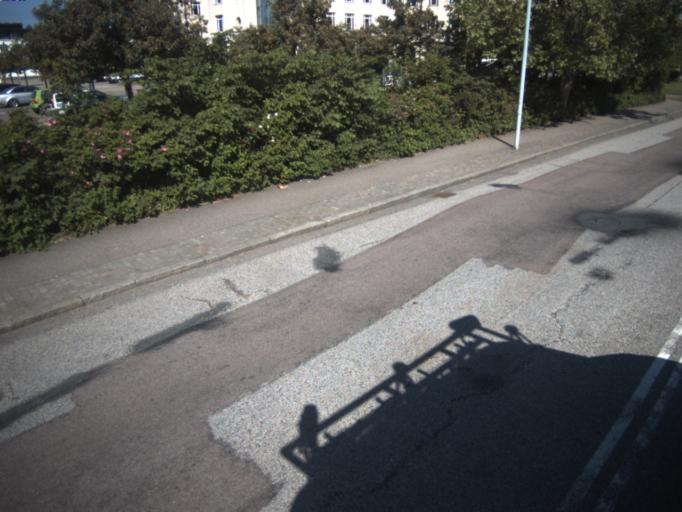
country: SE
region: Skane
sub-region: Helsingborg
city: Helsingborg
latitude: 56.0312
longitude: 12.7053
